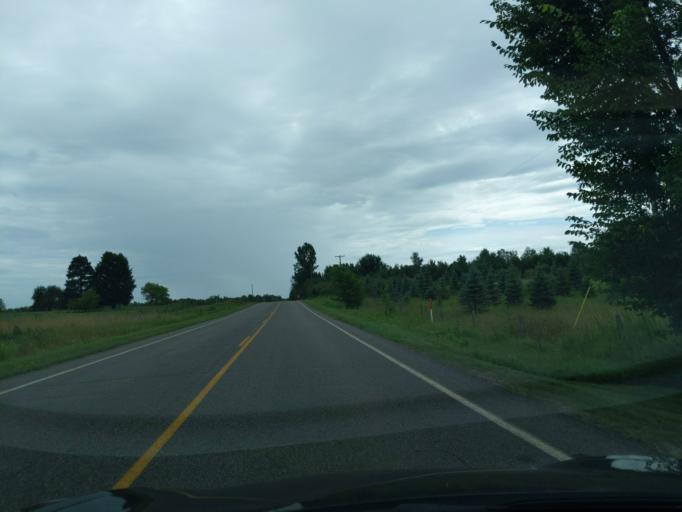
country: US
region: Michigan
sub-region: Clare County
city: Harrison
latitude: 44.0222
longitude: -84.9495
